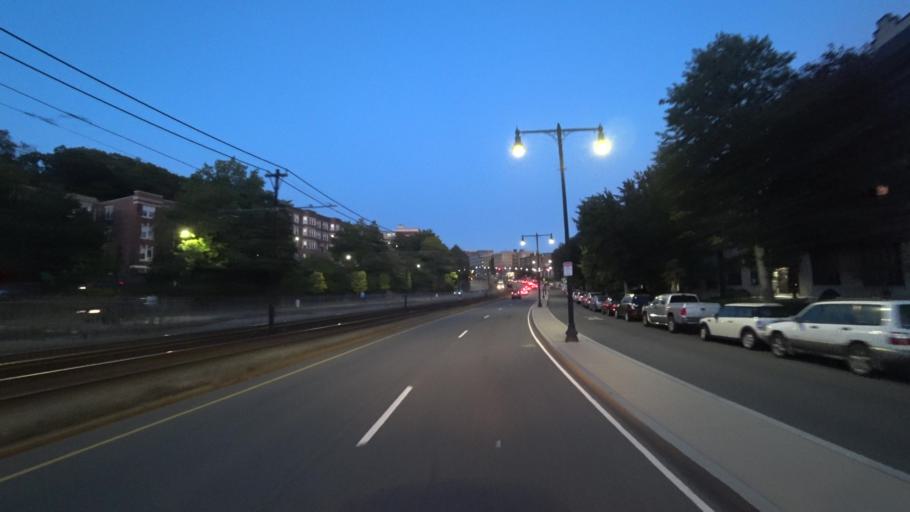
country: US
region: Massachusetts
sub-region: Norfolk County
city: Brookline
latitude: 42.3414
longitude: -71.1486
